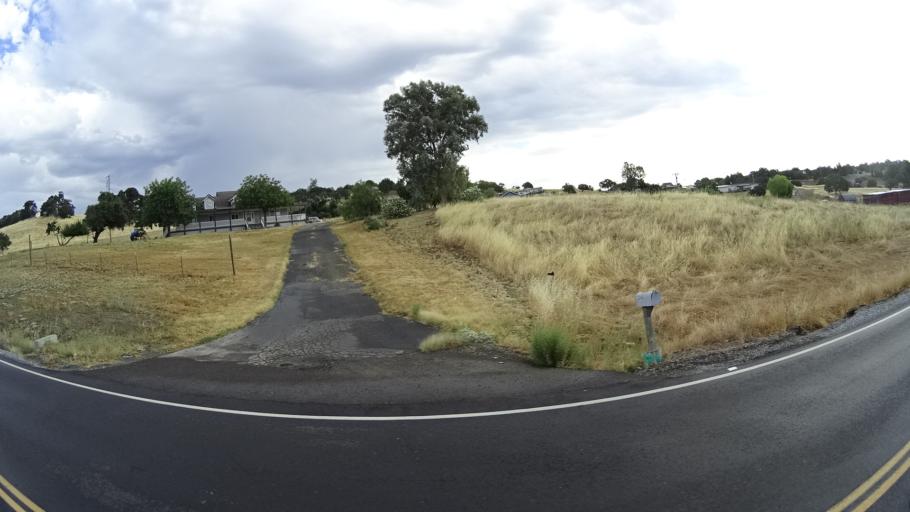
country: US
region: California
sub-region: Calaveras County
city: Copperopolis
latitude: 37.9219
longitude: -120.6326
